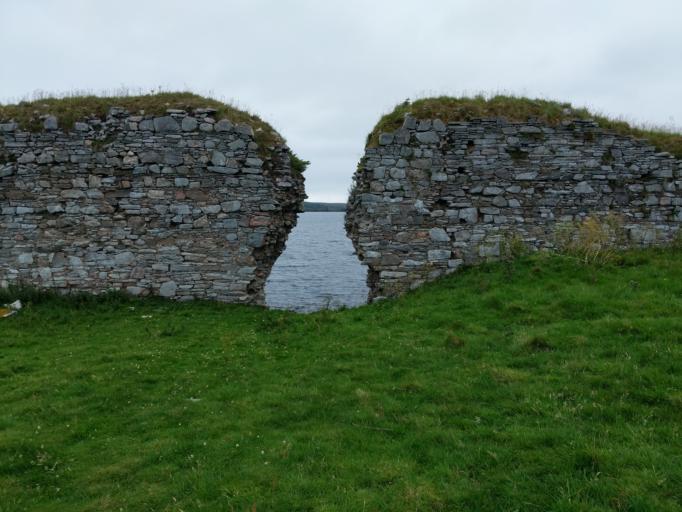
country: GB
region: Scotland
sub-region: Highland
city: Grantown on Spey
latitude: 57.4057
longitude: -3.7082
